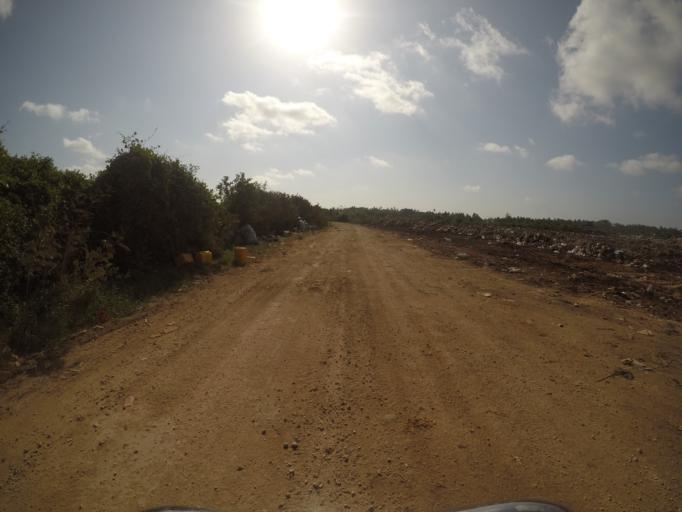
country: TZ
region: Zanzibar Central/South
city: Koani
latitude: -6.2182
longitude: 39.3299
